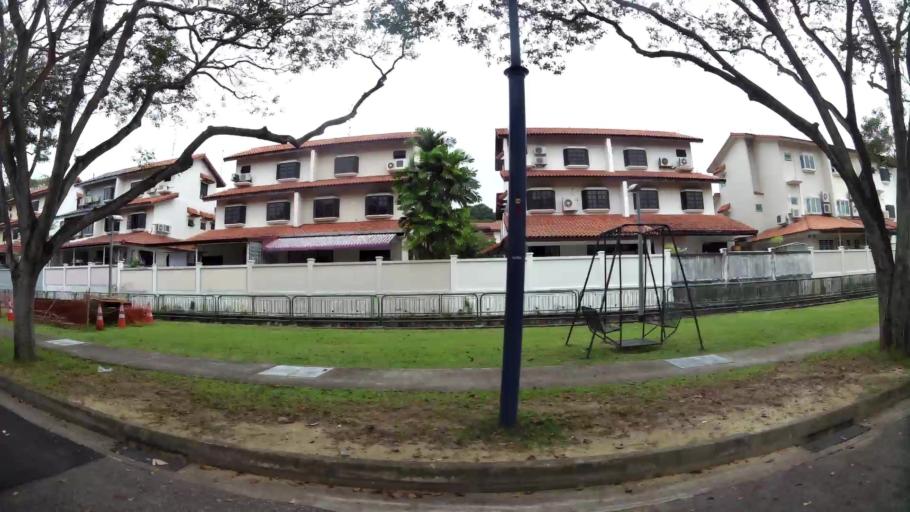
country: SG
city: Singapore
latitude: 1.3568
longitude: 103.8669
